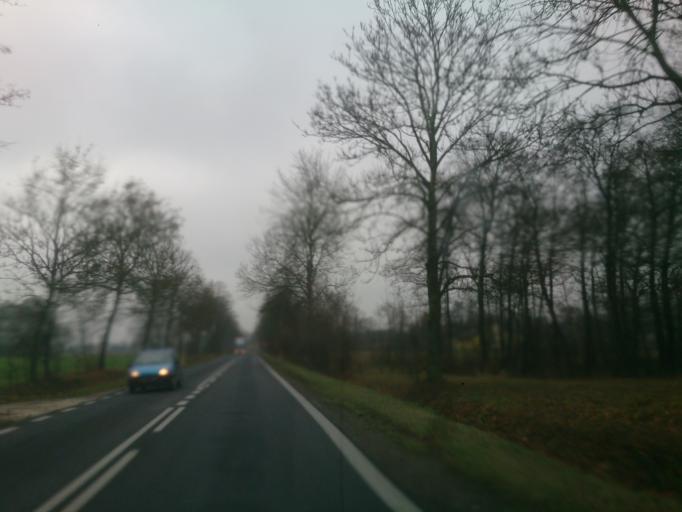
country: PL
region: Masovian Voivodeship
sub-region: Powiat sierpecki
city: Szczutowo
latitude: 52.9453
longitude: 19.5853
